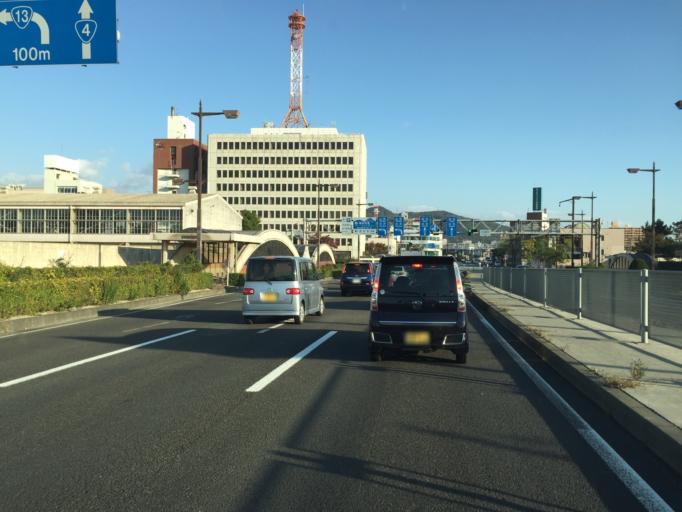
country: JP
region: Fukushima
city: Fukushima-shi
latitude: 37.7514
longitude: 140.4715
